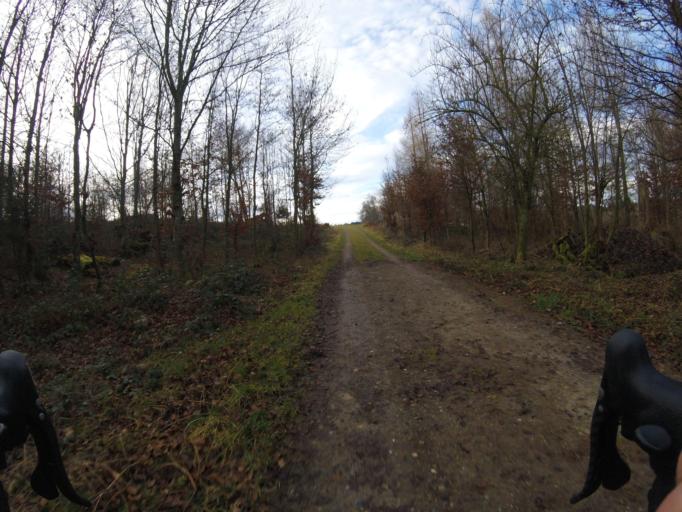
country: CH
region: Fribourg
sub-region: Sense District
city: Flamatt
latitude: 46.9099
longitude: 7.3398
